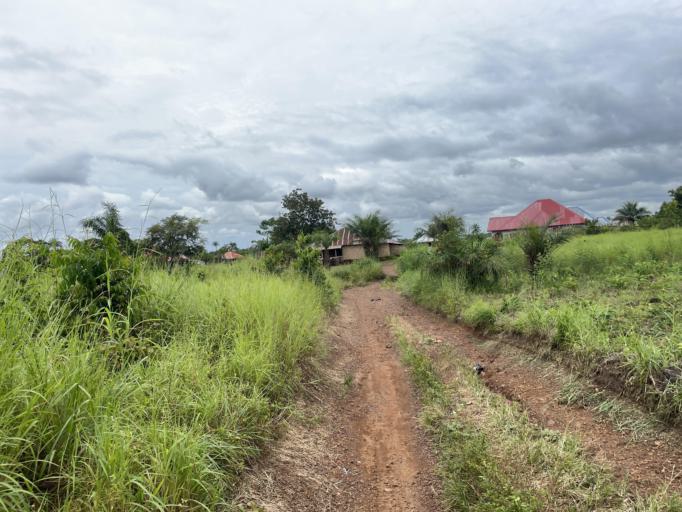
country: SL
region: Northern Province
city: Kambia
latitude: 9.1317
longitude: -12.9078
